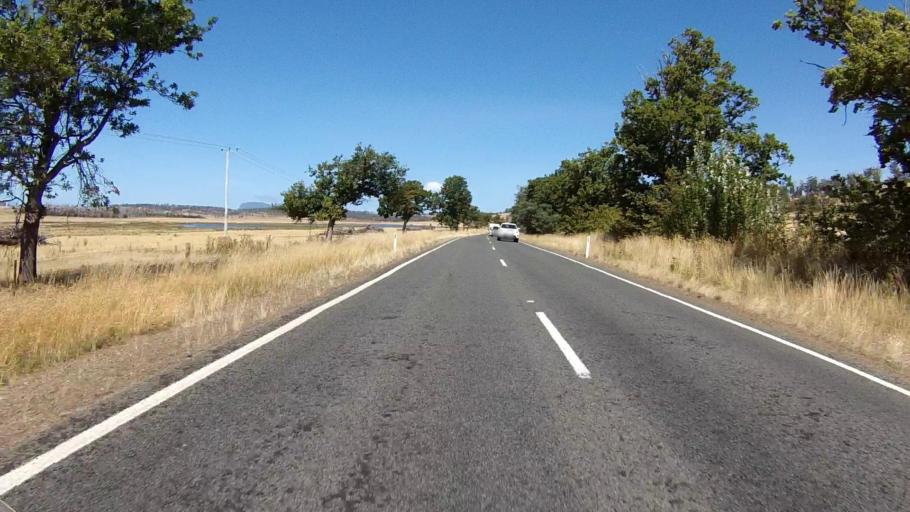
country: AU
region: Tasmania
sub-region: Sorell
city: Sorell
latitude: -42.4791
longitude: 147.9314
